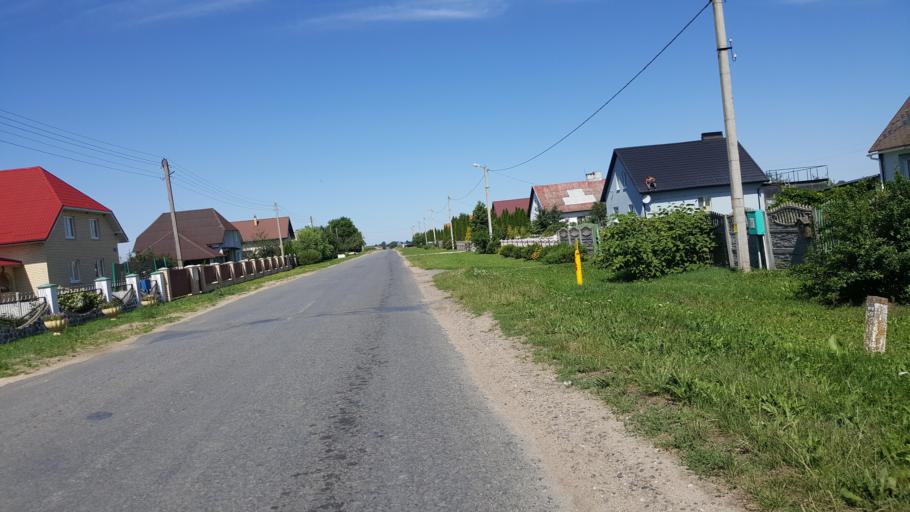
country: BY
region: Brest
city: Charnawchytsy
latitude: 52.2268
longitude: 23.7348
